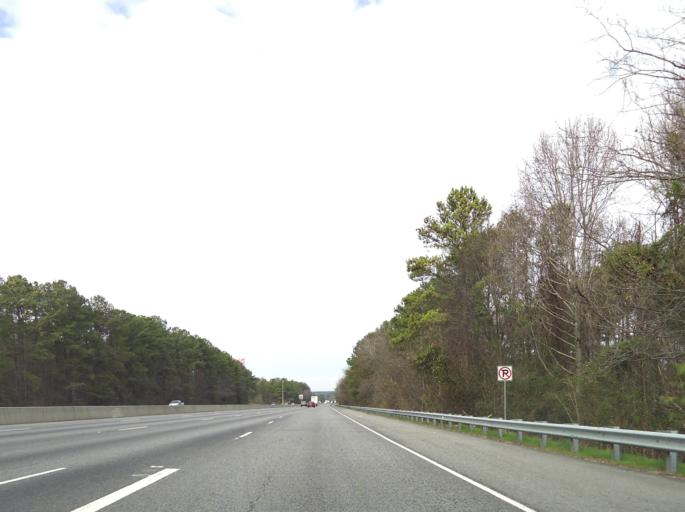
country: US
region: Georgia
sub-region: Bibb County
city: West Point
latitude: 32.8367
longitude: -83.7345
